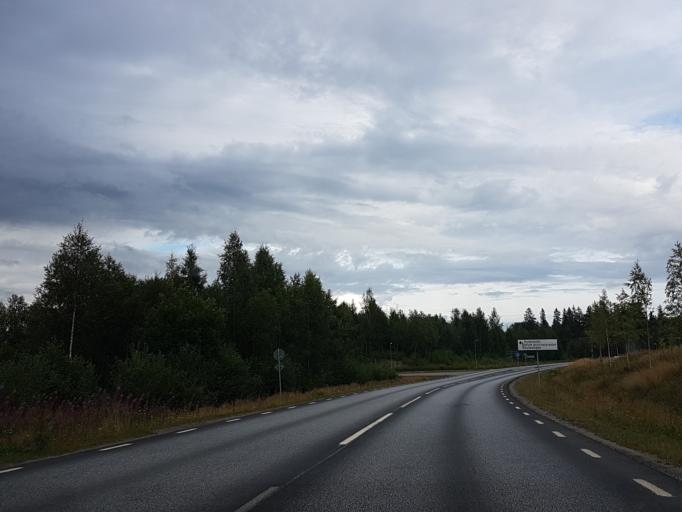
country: SE
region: Vaesterbotten
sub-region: Umea Kommun
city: Ersmark
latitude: 63.8074
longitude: 20.3671
